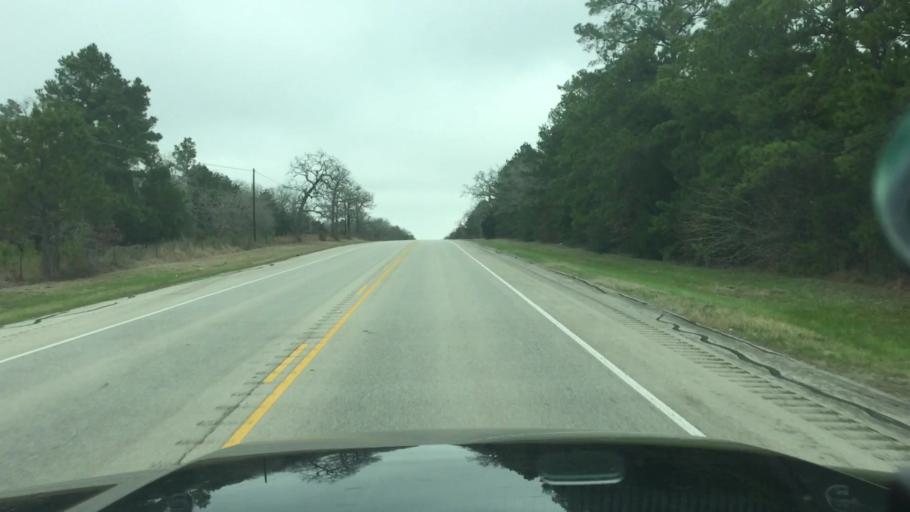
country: US
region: Texas
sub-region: Lee County
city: Giddings
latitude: 30.0715
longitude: -96.9168
